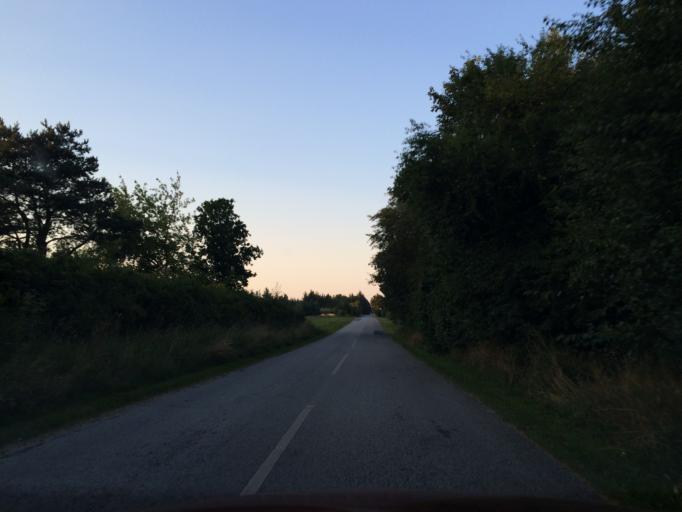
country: DK
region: Central Jutland
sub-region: Silkeborg Kommune
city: Svejbaek
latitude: 56.2146
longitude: 9.6596
